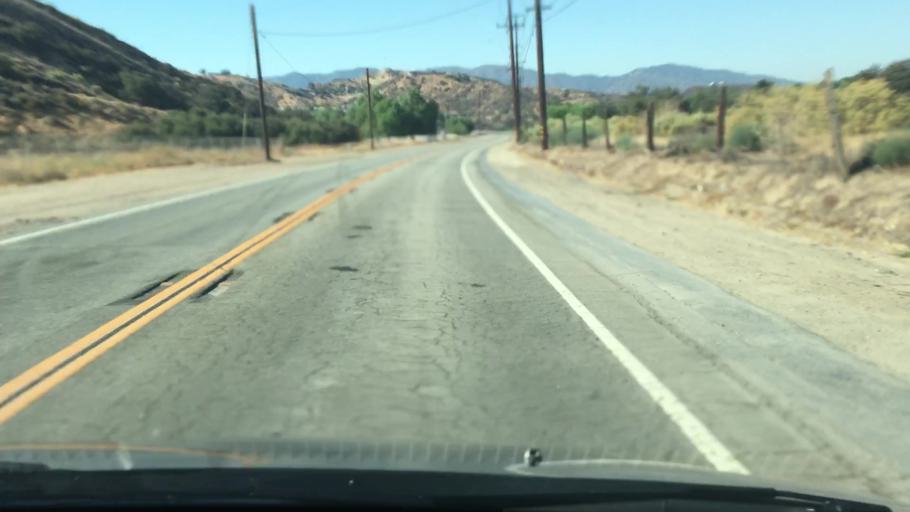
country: US
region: California
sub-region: Los Angeles County
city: Agua Dulce
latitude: 34.4599
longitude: -118.4210
